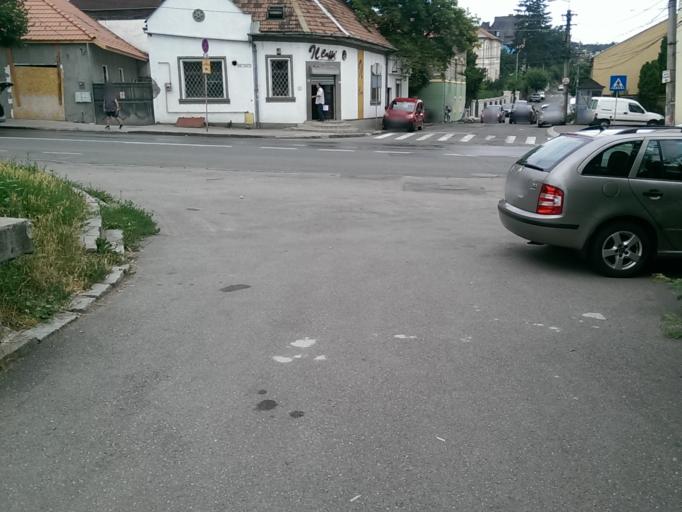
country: RO
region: Cluj
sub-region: Municipiul Cluj-Napoca
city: Cluj-Napoca
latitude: 46.7672
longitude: 23.6027
